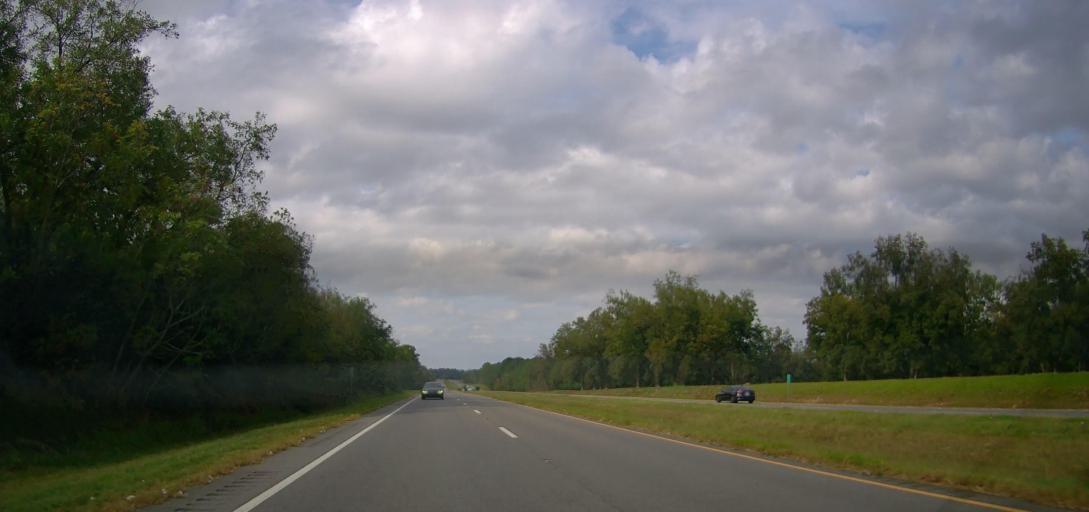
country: US
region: Georgia
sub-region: Thomas County
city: Meigs
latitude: 31.0357
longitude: -84.0651
